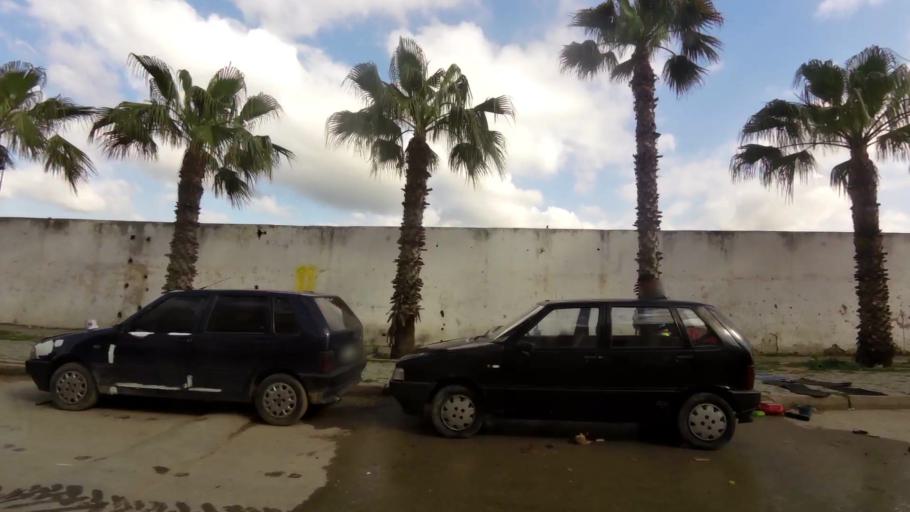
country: MA
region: Chaouia-Ouardigha
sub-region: Settat Province
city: Berrechid
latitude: 33.2724
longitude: -7.5677
